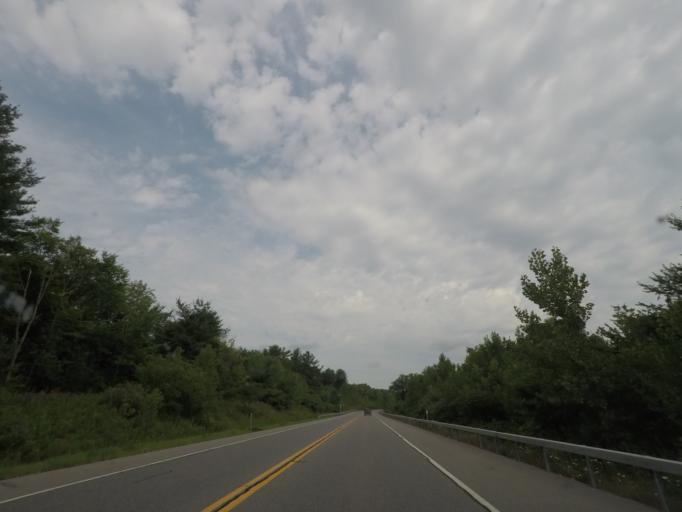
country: US
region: New York
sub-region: Saratoga County
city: Country Knolls
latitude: 42.9390
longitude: -73.8017
